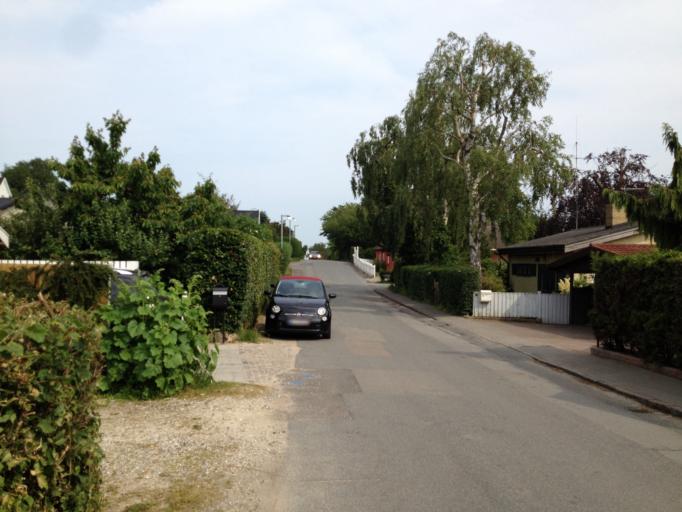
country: DK
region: Capital Region
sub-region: Fredensborg Kommune
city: Humlebaek
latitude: 55.9529
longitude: 12.5272
